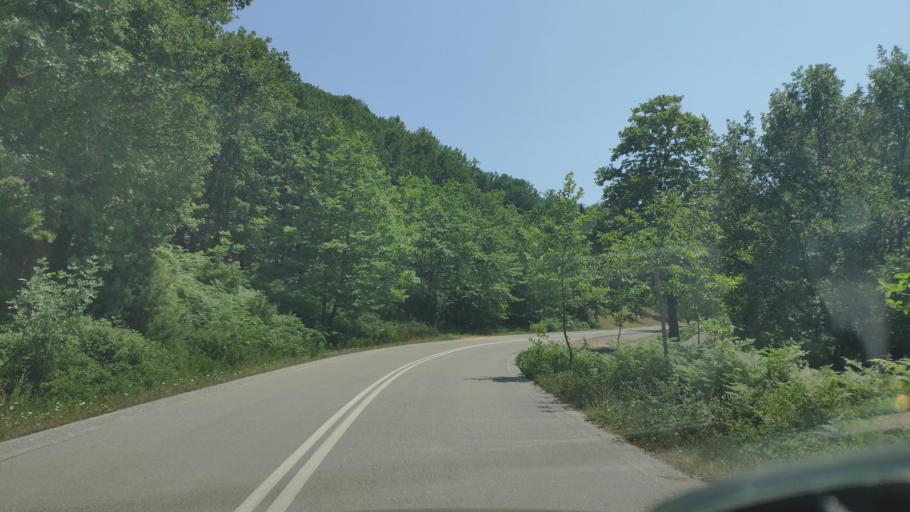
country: GR
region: Epirus
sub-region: Nomos Artas
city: Ano Kalentini
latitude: 39.2422
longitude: 21.2087
